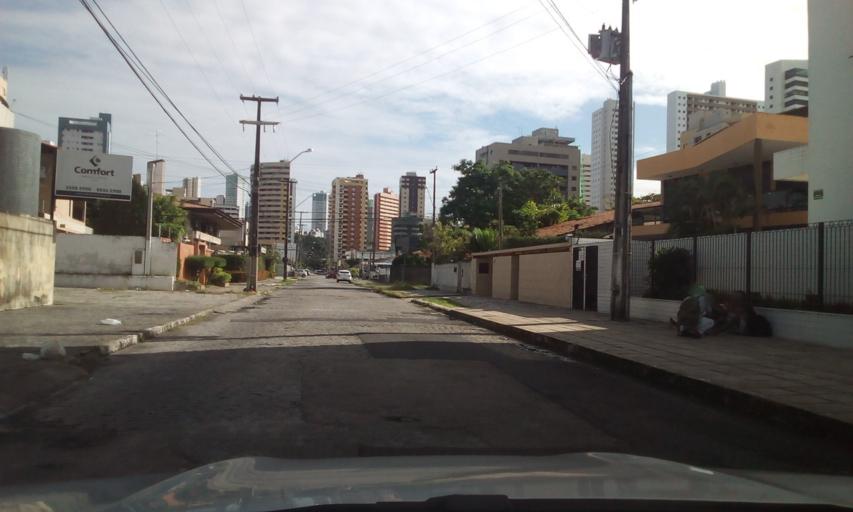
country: BR
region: Paraiba
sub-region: Joao Pessoa
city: Joao Pessoa
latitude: -7.1080
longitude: -34.8301
